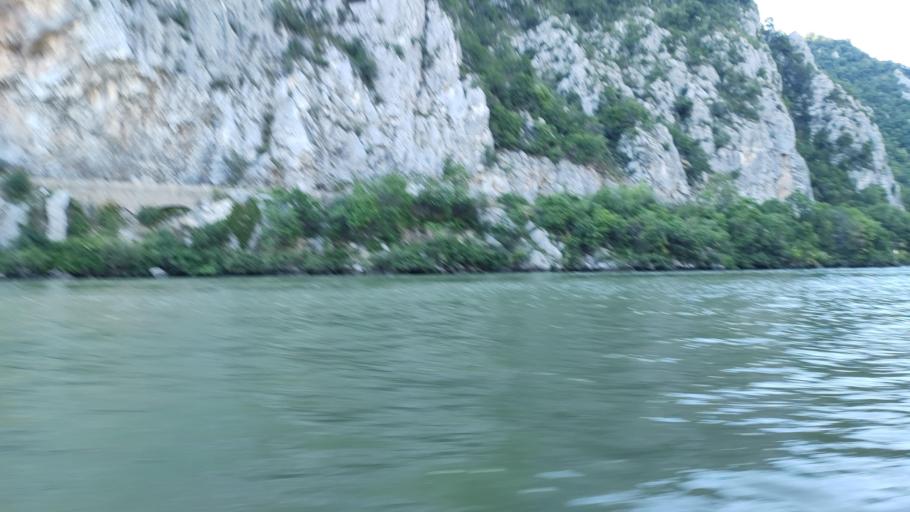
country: RO
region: Mehedinti
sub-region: Comuna Dubova
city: Dubova
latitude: 44.6308
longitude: 22.2851
